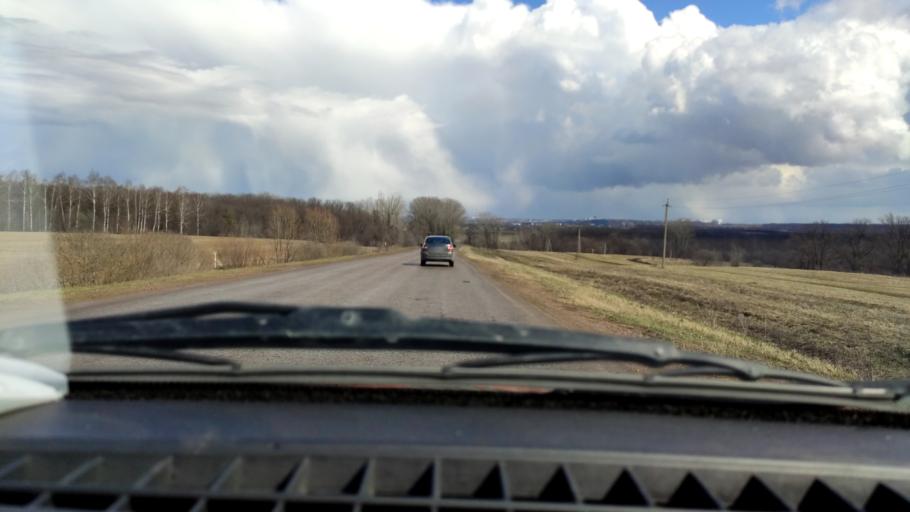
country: RU
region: Bashkortostan
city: Mikhaylovka
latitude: 54.8329
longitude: 55.9227
